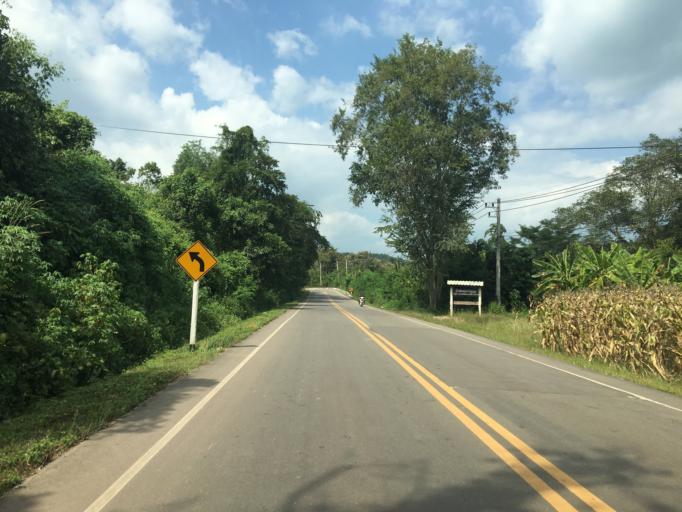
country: TH
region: Nan
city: Nan
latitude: 18.8587
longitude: 100.6476
